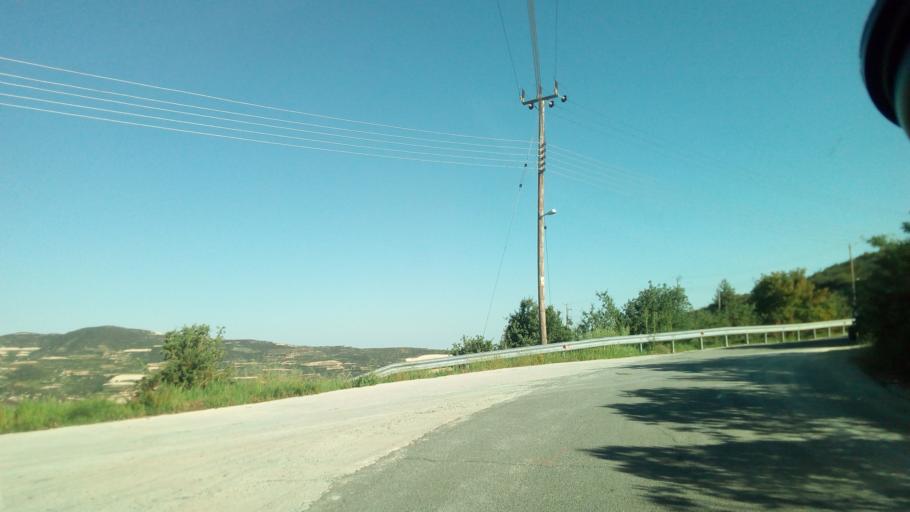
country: CY
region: Limassol
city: Pachna
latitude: 34.8632
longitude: 32.8014
